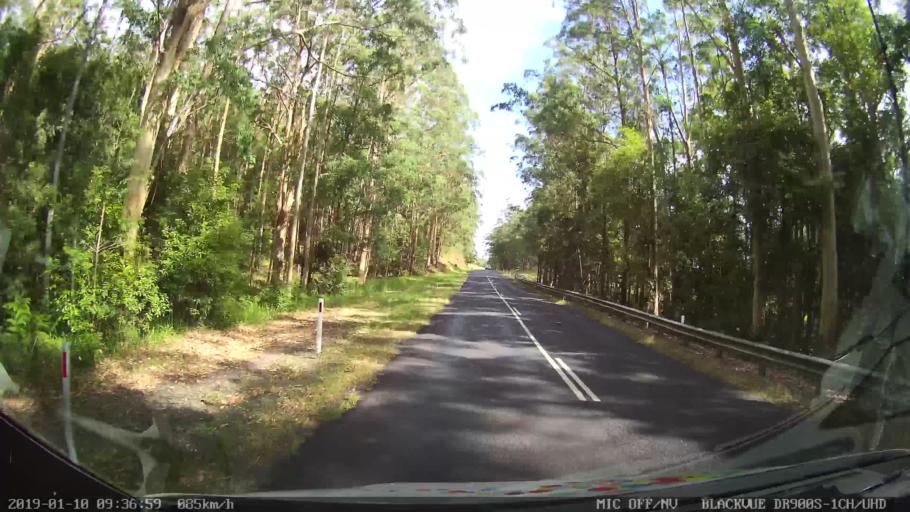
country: AU
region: New South Wales
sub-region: Coffs Harbour
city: Nana Glen
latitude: -30.1928
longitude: 153.0124
